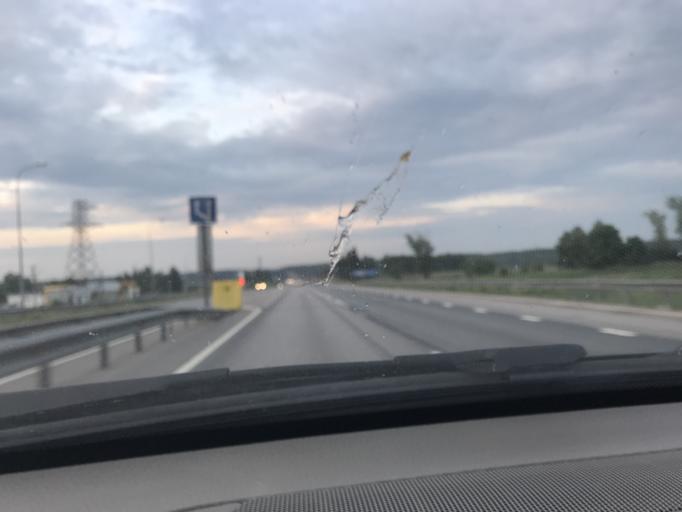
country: RU
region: Kaluga
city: Obninsk
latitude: 55.0412
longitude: 36.5952
